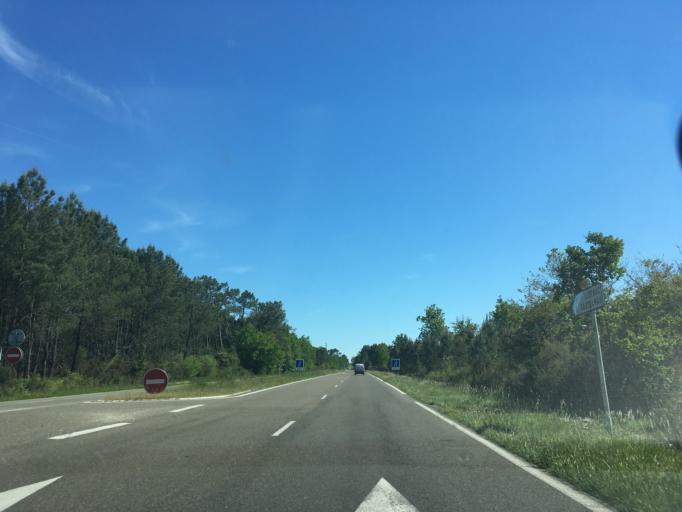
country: FR
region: Aquitaine
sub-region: Departement de la Gironde
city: Listrac-Medoc
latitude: 45.1039
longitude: -0.8038
